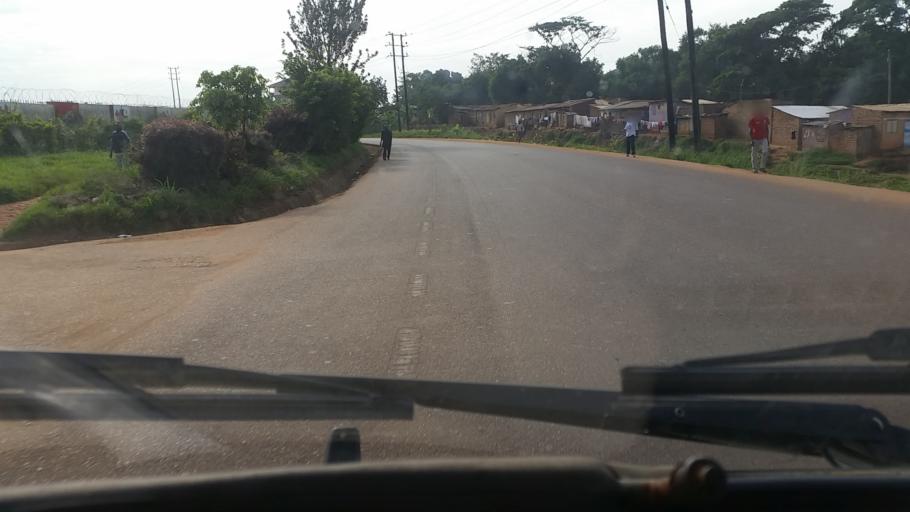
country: UG
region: Central Region
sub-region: Wakiso District
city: Kireka
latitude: 0.3454
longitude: 32.6587
